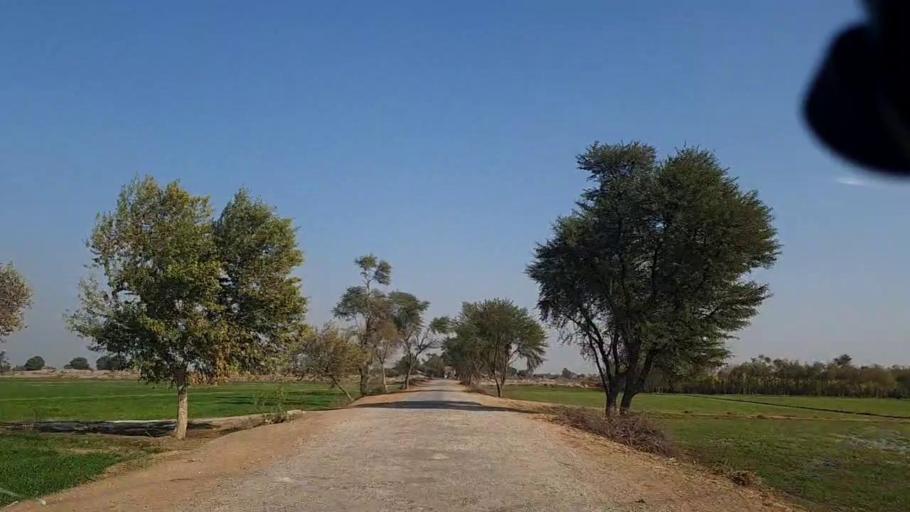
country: PK
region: Sindh
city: Khanpur
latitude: 27.6861
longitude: 69.4924
